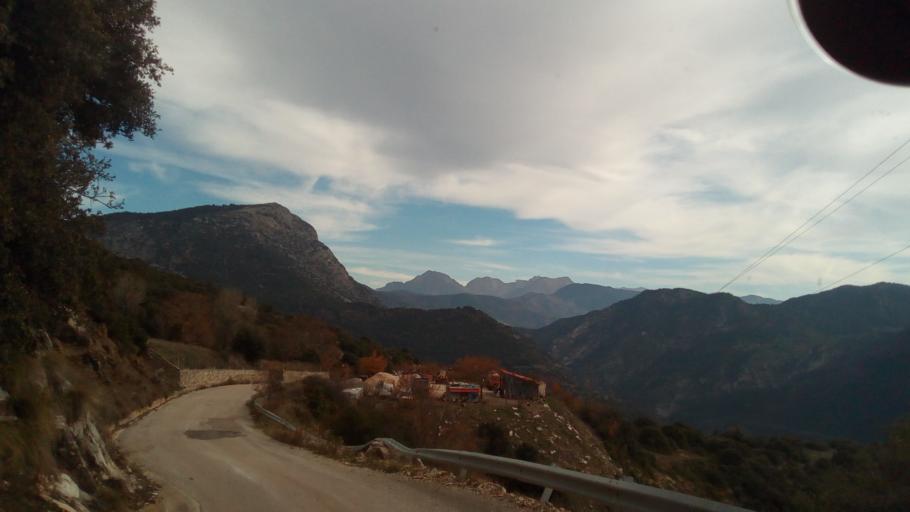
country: GR
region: West Greece
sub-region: Nomos Aitolias kai Akarnanias
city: Thermo
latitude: 38.6746
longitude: 21.8909
